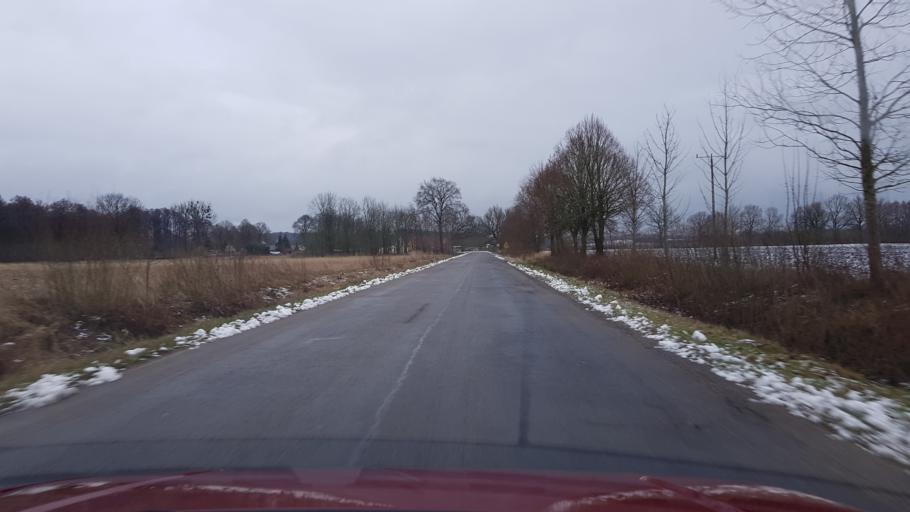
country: PL
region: West Pomeranian Voivodeship
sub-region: Powiat lobeski
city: Resko
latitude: 53.8485
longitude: 15.3525
